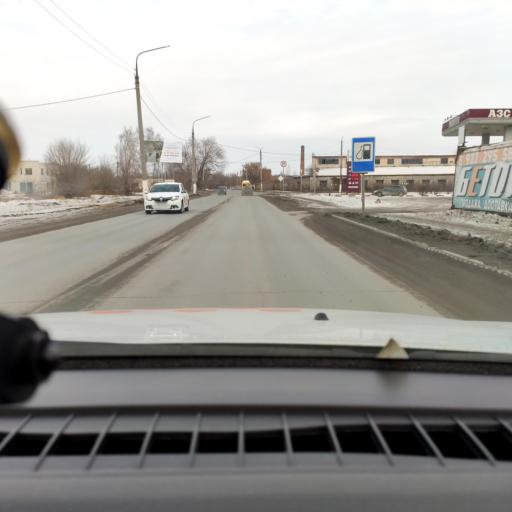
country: RU
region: Samara
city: Chapayevsk
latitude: 52.9651
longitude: 49.6930
